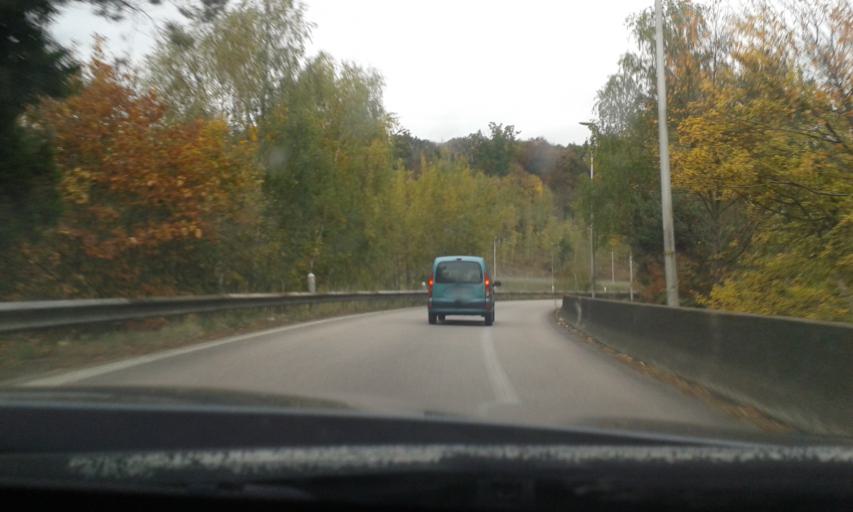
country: FR
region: Haute-Normandie
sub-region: Departement de la Seine-Maritime
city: Oissel
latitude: 49.3381
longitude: 1.0726
